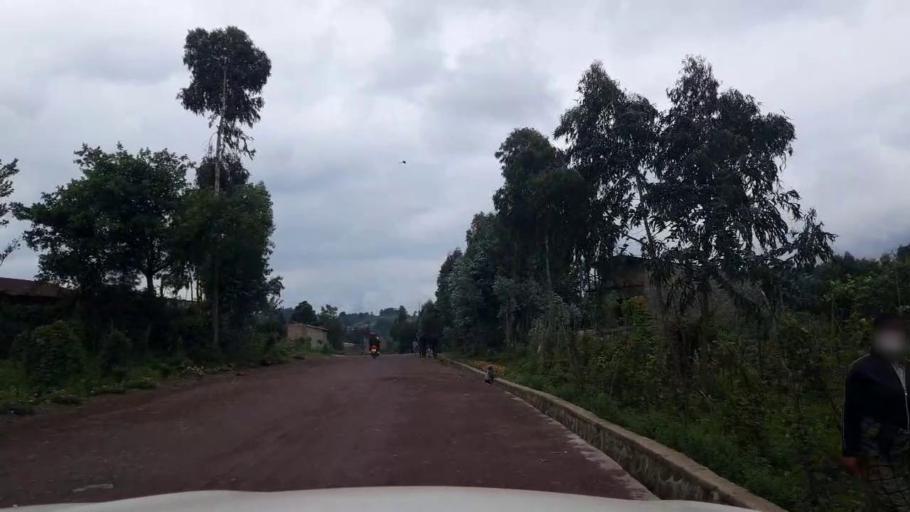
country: RW
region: Northern Province
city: Musanze
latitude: -1.5915
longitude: 29.4580
